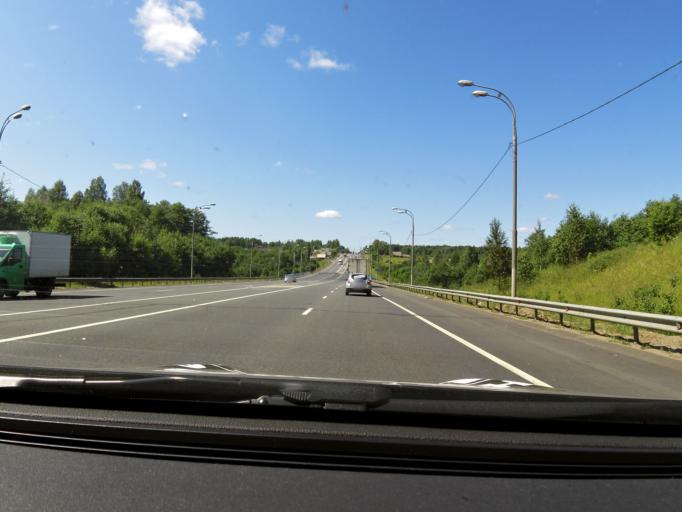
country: RU
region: Novgorod
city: Kresttsy
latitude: 58.1196
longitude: 32.8121
